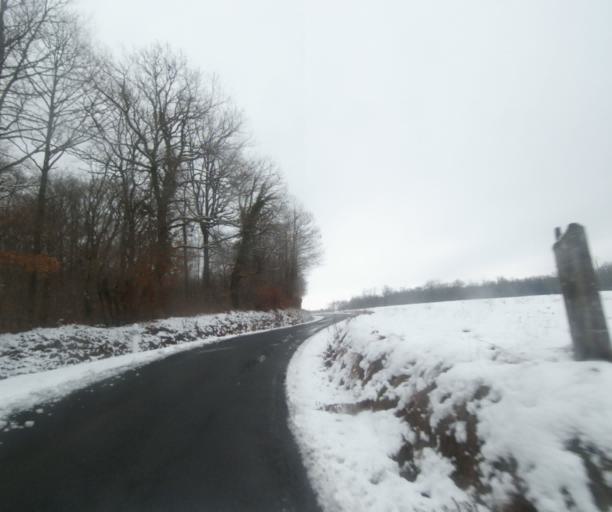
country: FR
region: Champagne-Ardenne
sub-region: Departement de la Haute-Marne
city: Laneuville-a-Remy
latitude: 48.4704
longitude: 4.8904
